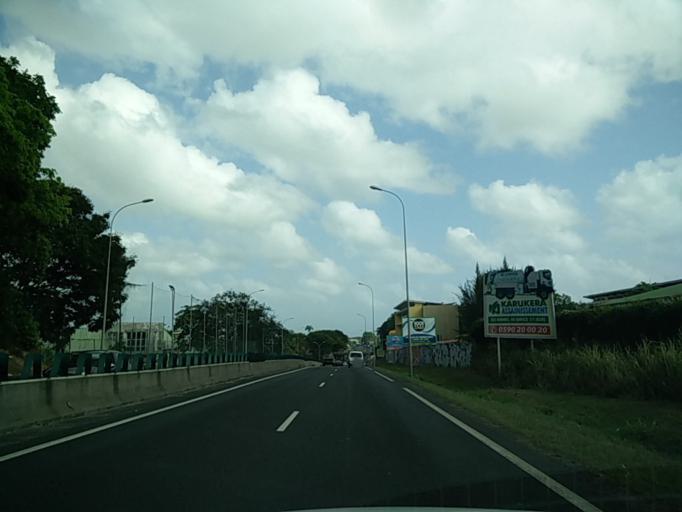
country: GP
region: Guadeloupe
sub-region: Guadeloupe
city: Pointe-a-Pitre
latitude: 16.2459
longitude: -61.5251
